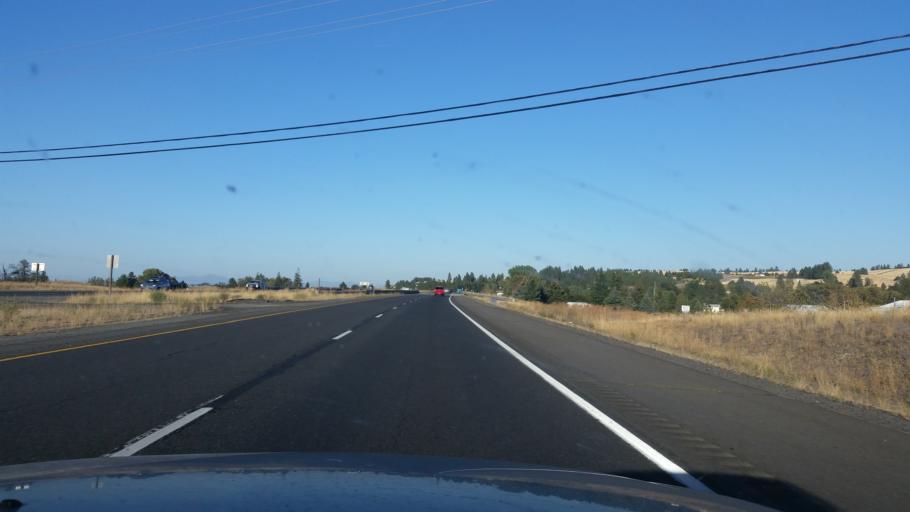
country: US
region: Washington
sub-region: Spokane County
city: Fairchild Air Force Base
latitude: 47.5594
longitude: -117.6078
